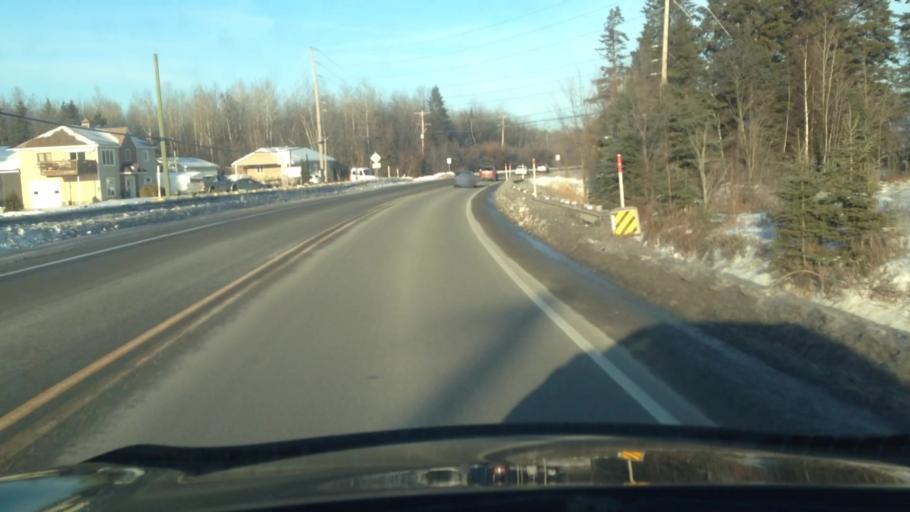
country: CA
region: Quebec
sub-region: Laurentides
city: Sainte-Sophie
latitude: 45.8291
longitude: -73.8855
